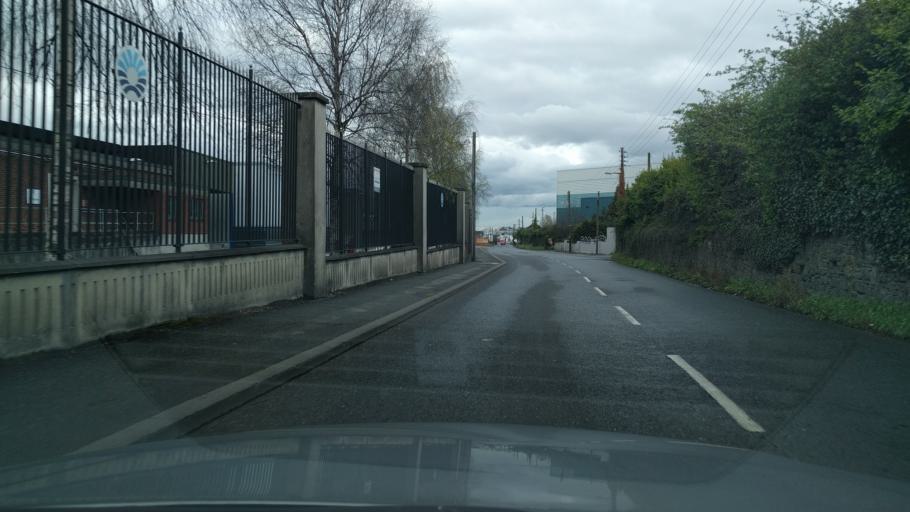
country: IE
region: Leinster
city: Ballyfermot
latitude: 53.3196
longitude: -6.3562
